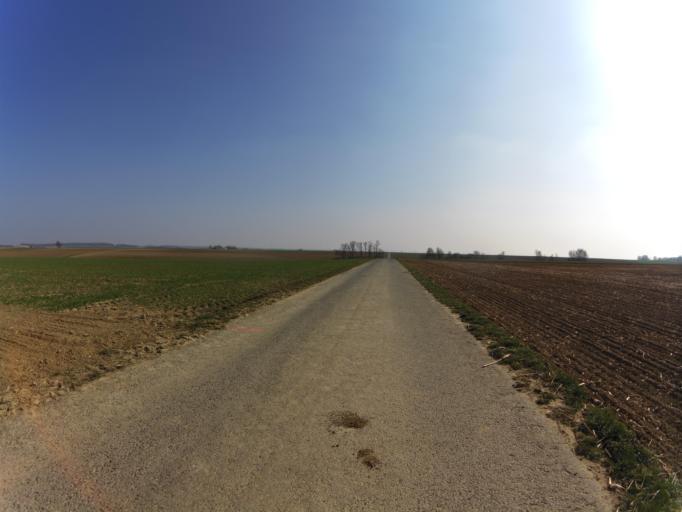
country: DE
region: Bavaria
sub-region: Regierungsbezirk Unterfranken
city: Gaukonigshofen
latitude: 49.6563
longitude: 9.9887
